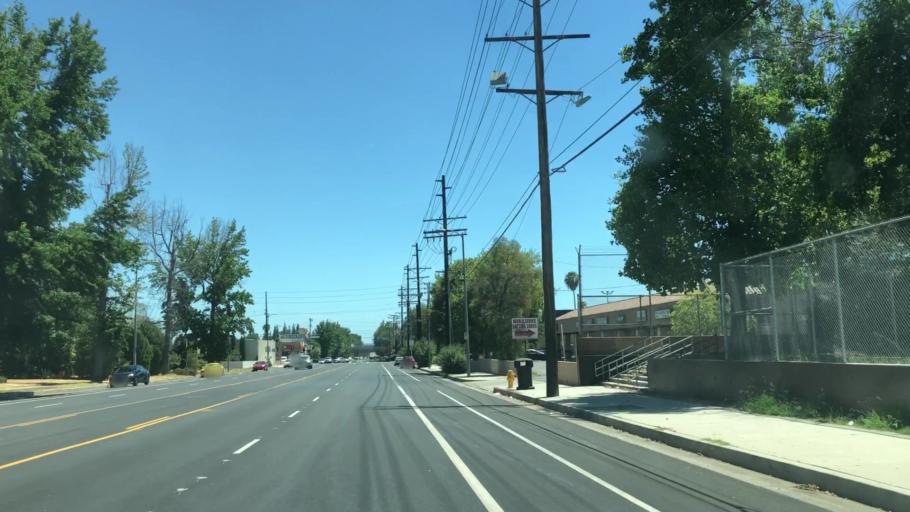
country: US
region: California
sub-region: Los Angeles County
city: San Fernando
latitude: 34.2739
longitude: -118.4848
